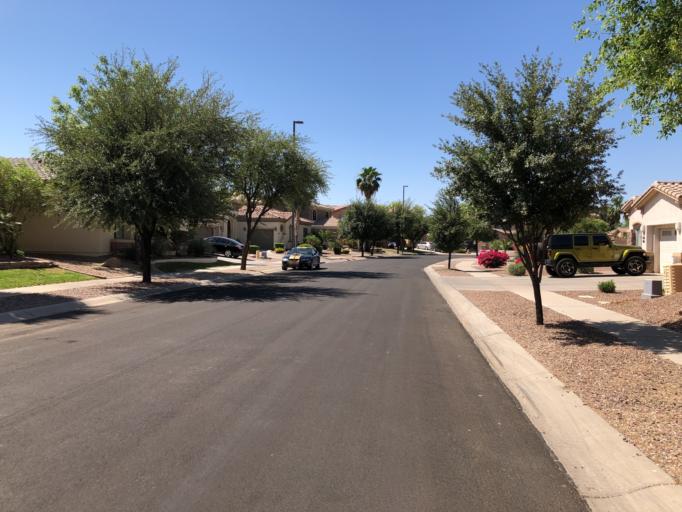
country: US
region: Arizona
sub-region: Maricopa County
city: Queen Creek
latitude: 33.2679
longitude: -111.6887
